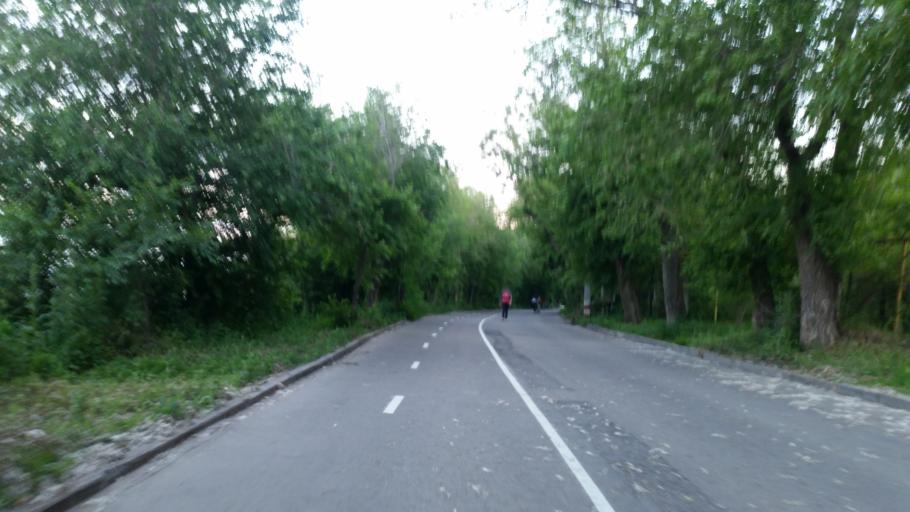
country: RU
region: Ulyanovsk
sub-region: Ulyanovskiy Rayon
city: Ulyanovsk
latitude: 54.3231
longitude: 48.4098
